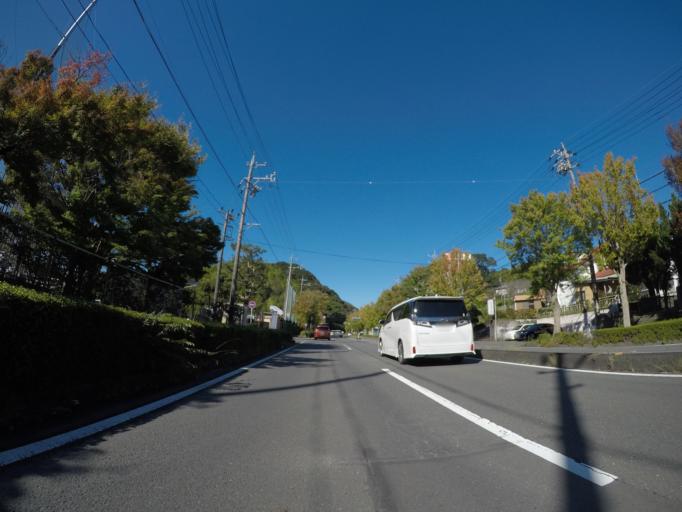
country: JP
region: Shizuoka
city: Fujieda
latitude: 34.8666
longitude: 138.2353
